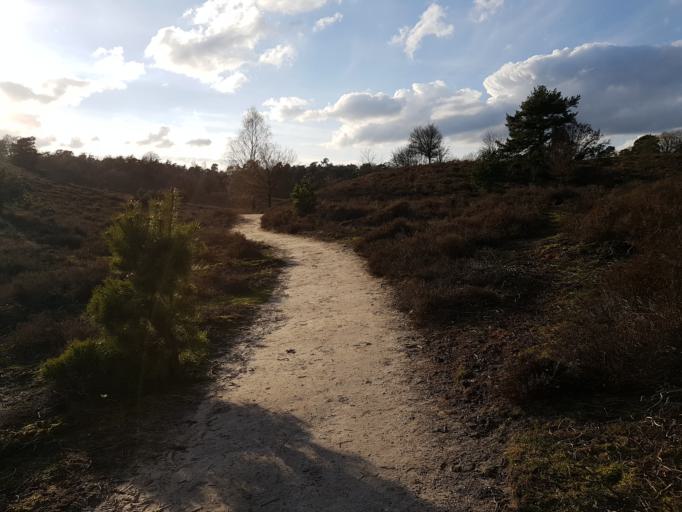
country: NL
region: Gelderland
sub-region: Gemeente Rheden
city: Rheden
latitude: 52.0271
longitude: 6.0109
